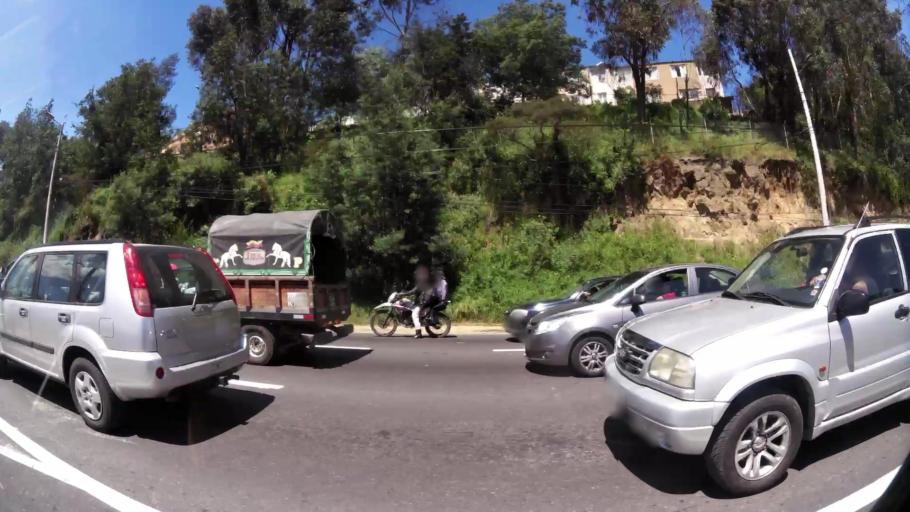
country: EC
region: Pichincha
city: Quito
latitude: -0.0963
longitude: -78.4673
